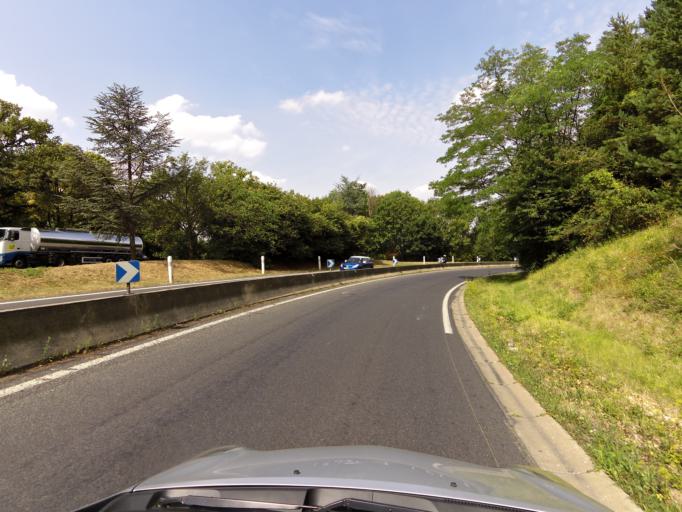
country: FR
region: Champagne-Ardenne
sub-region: Departement de la Marne
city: Rilly-la-Montagne
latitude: 49.1598
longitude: 4.0084
